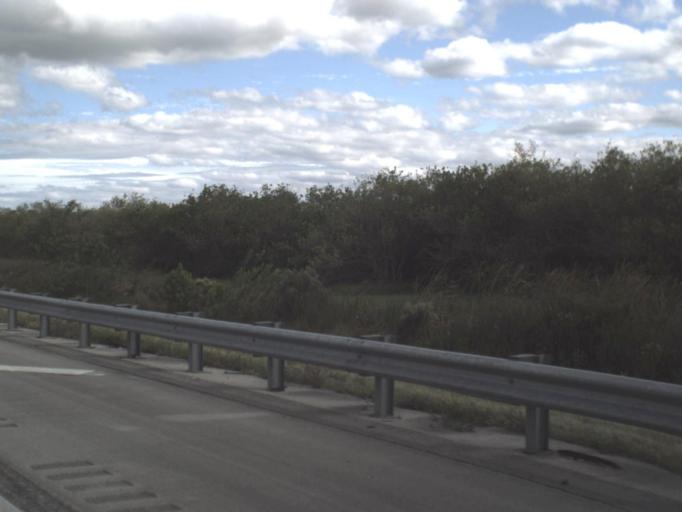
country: US
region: Florida
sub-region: Saint Lucie County
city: Lakewood Park
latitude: 27.4849
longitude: -80.5226
